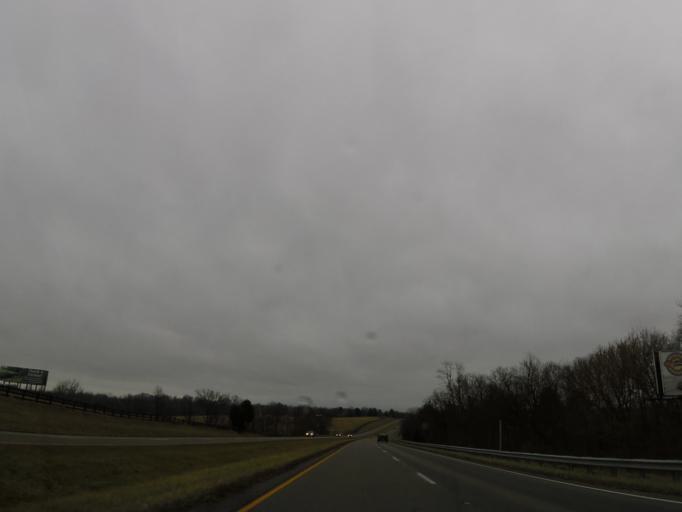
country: US
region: Kentucky
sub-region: Lincoln County
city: Stanford
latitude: 37.5852
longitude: -84.7148
